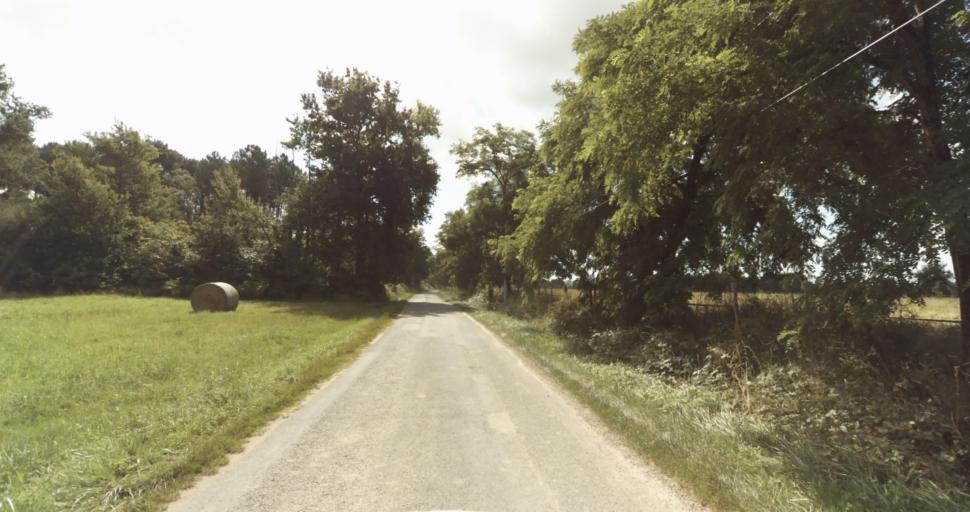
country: FR
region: Aquitaine
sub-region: Departement de la Gironde
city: Bazas
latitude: 44.4590
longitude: -0.1990
